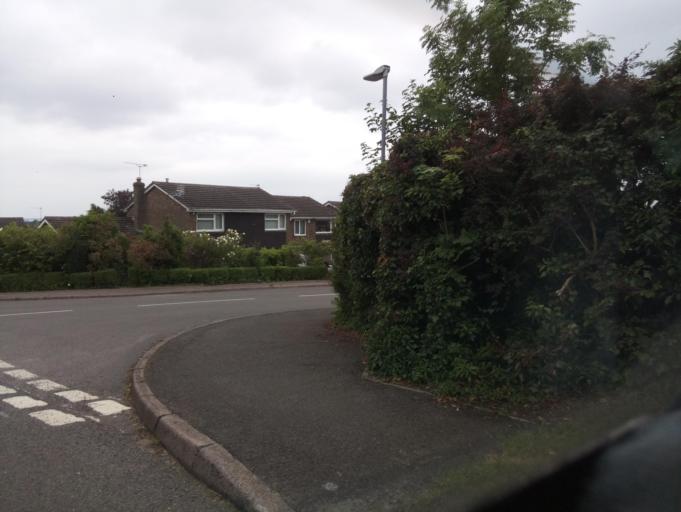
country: GB
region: England
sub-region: District of Rutland
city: Oakham
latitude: 52.6711
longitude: -0.7485
